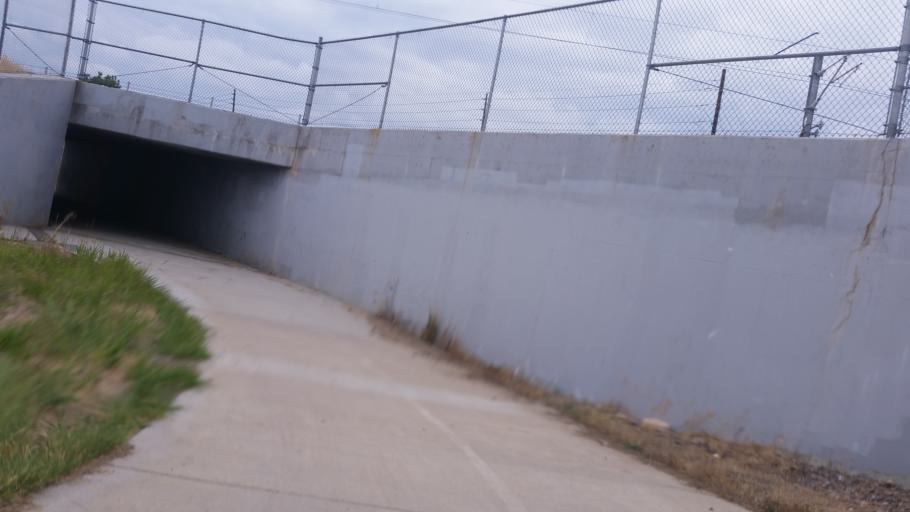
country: US
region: Colorado
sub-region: Adams County
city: Twin Lakes
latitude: 39.8157
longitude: -105.0150
